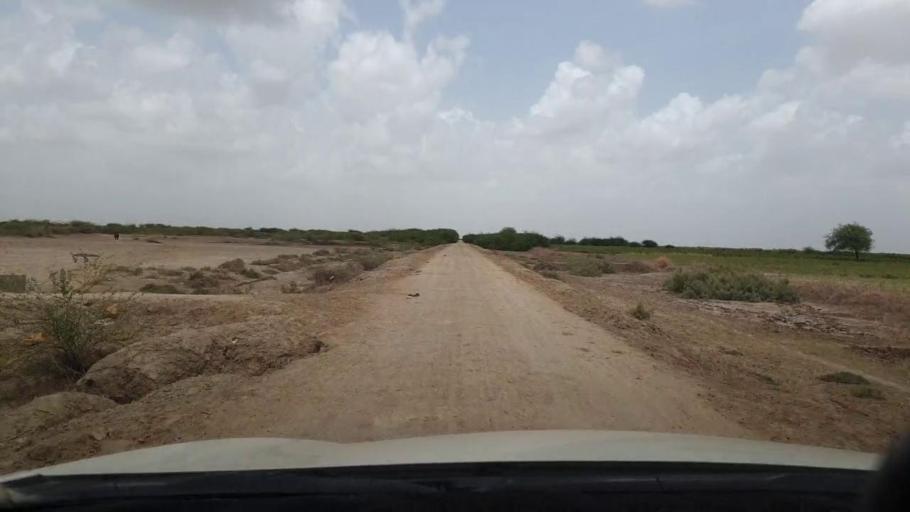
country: PK
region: Sindh
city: Kadhan
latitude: 24.3604
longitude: 68.9412
